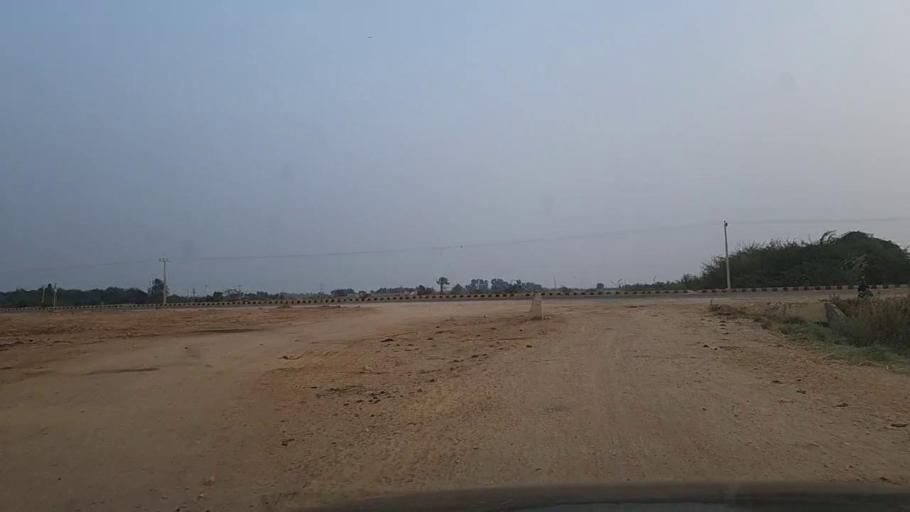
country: PK
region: Sindh
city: Gharo
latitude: 24.7344
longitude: 67.6959
